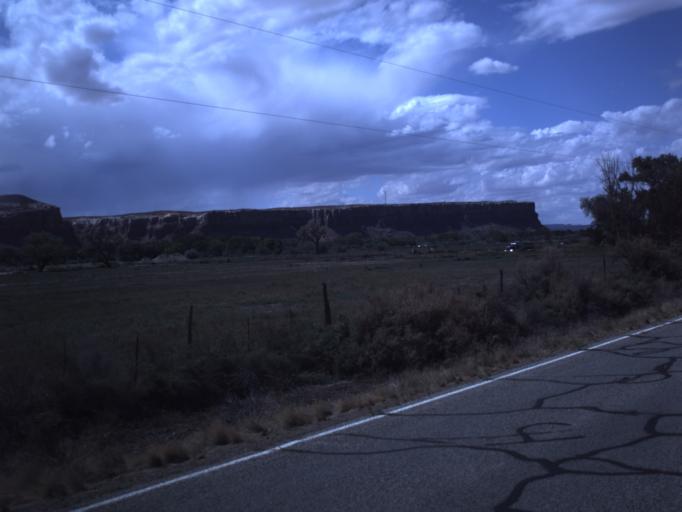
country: US
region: Utah
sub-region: San Juan County
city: Blanding
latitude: 37.2847
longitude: -109.5297
